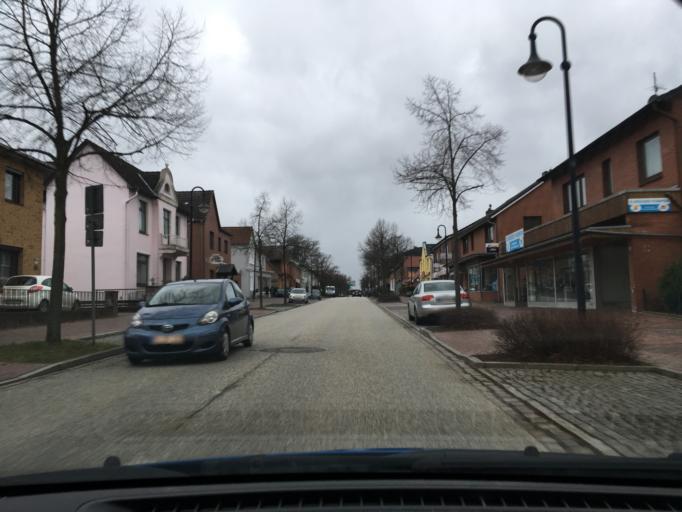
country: DE
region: Schleswig-Holstein
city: Schwarzenbek
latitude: 53.5011
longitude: 10.4866
